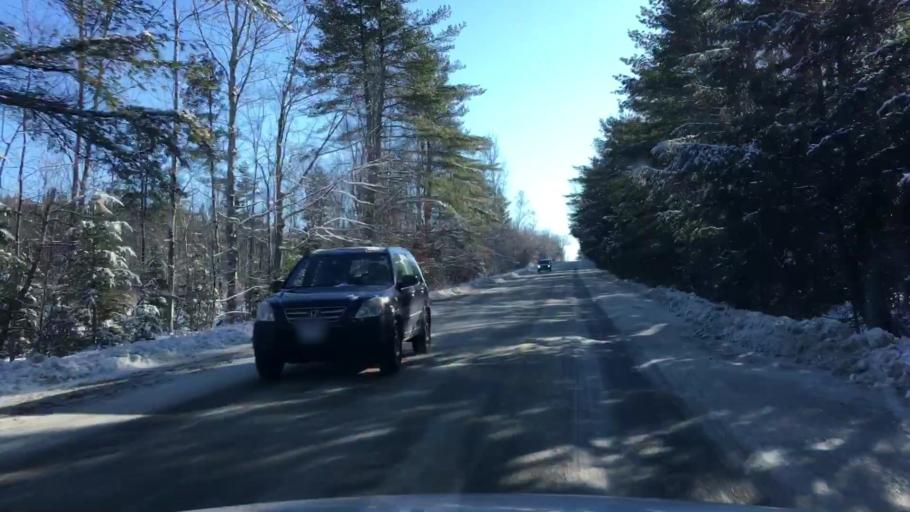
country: US
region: Maine
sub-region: Kennebec County
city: Readfield
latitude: 44.3506
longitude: -69.9907
